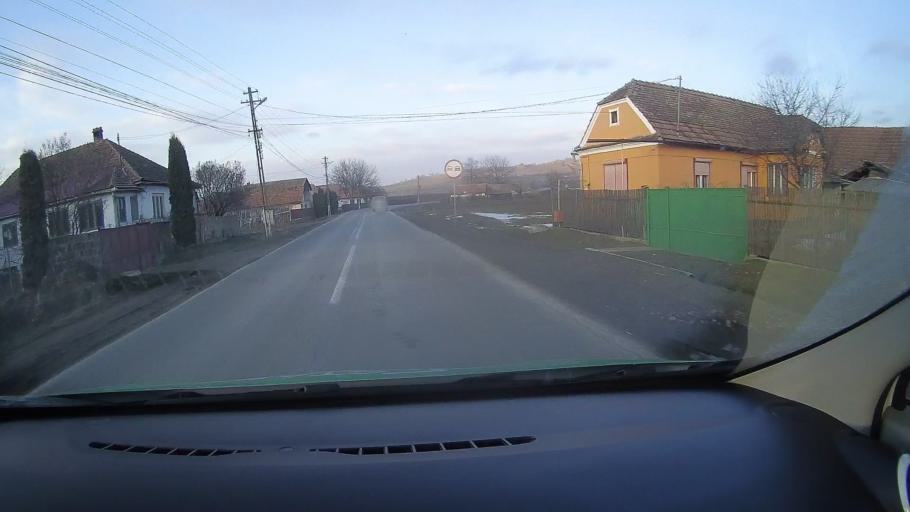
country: RO
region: Mures
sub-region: Comuna Vanatori
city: Vanatori
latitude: 46.2458
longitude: 24.9240
